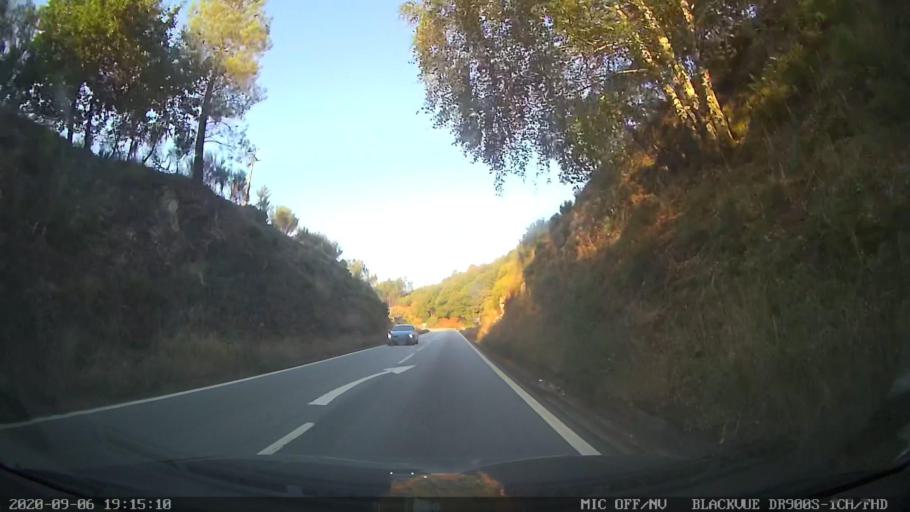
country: PT
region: Porto
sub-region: Baiao
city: Valadares
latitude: 41.2020
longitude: -7.9671
